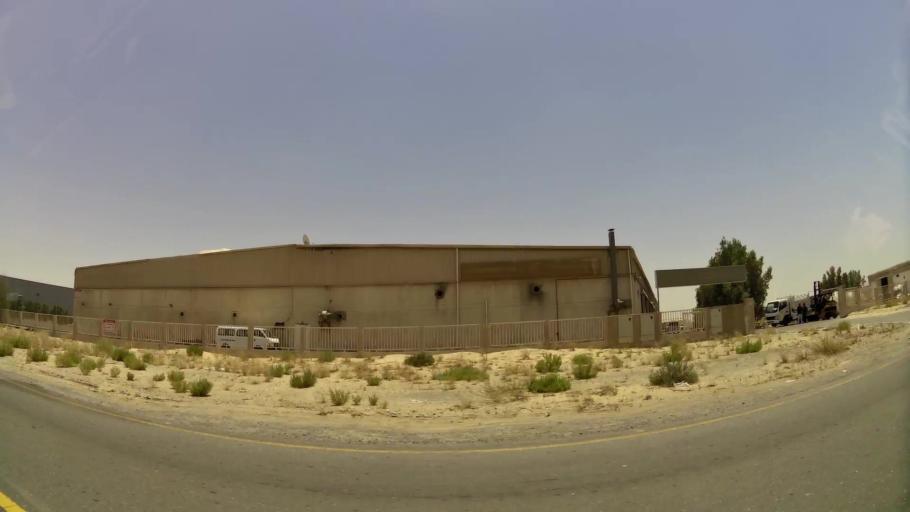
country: AE
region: Dubai
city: Dubai
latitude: 24.9846
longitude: 55.1681
